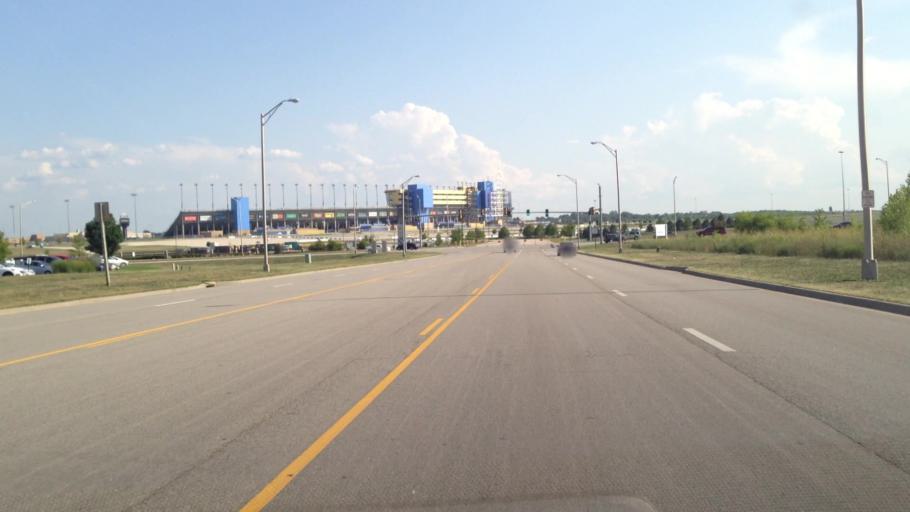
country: US
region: Kansas
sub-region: Wyandotte County
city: Edwardsville
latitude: 39.1308
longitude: -94.8343
